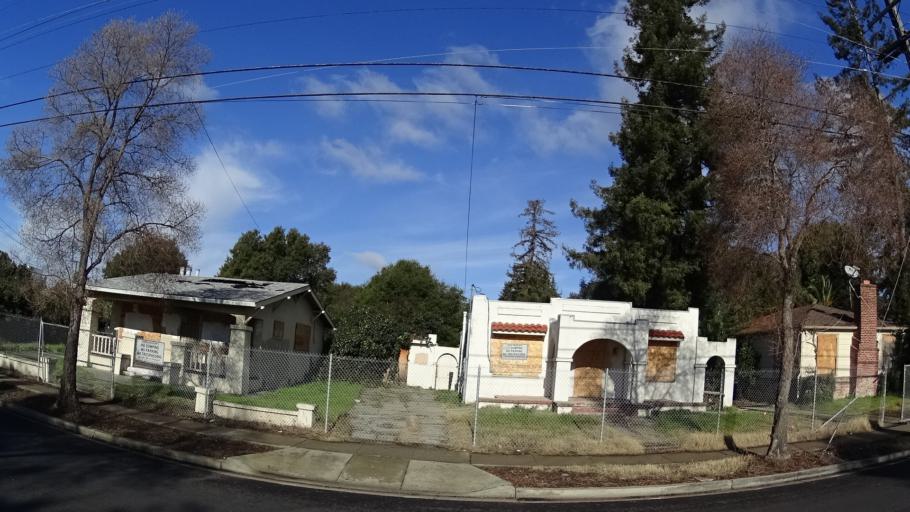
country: US
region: California
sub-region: Alameda County
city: Hayward
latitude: 37.6780
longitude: -122.0754
